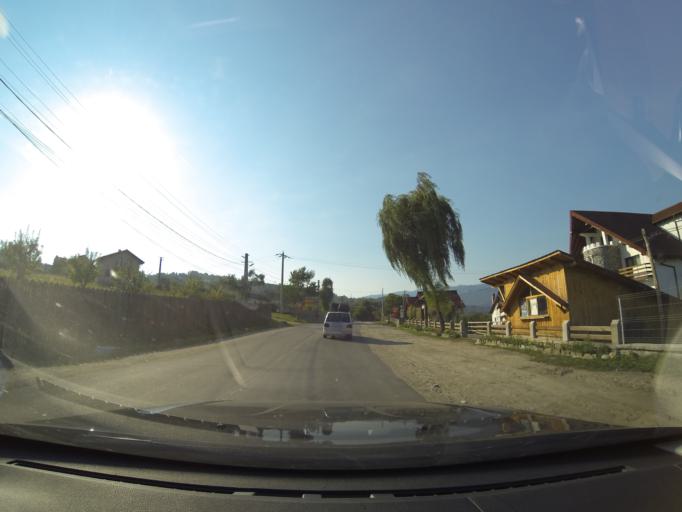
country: RO
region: Arges
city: Poenari
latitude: 45.3087
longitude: 24.6479
